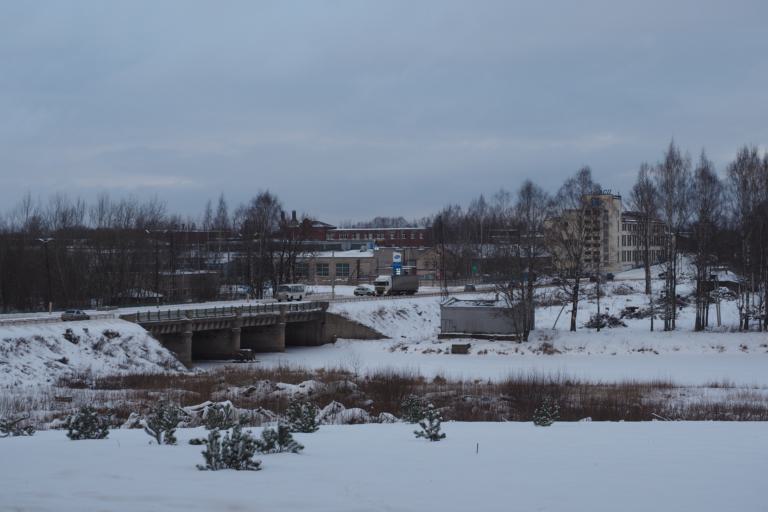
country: RU
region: Tverskaya
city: Bezhetsk
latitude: 57.7920
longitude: 36.6911
